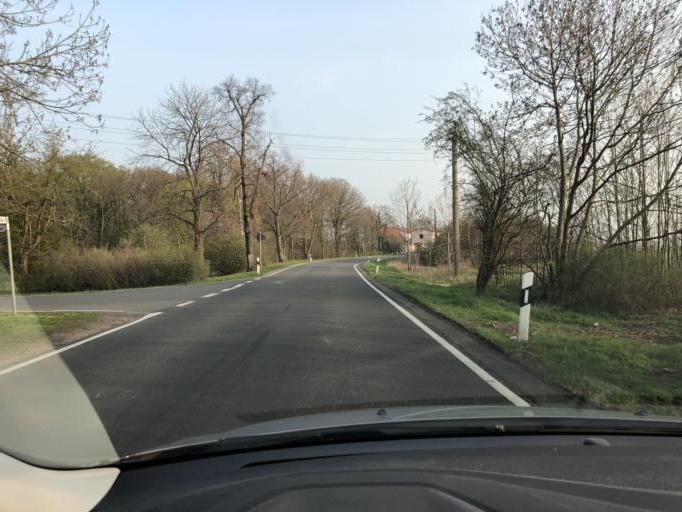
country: DE
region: Saxony-Anhalt
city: Roitzsch
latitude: 51.5343
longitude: 12.2887
